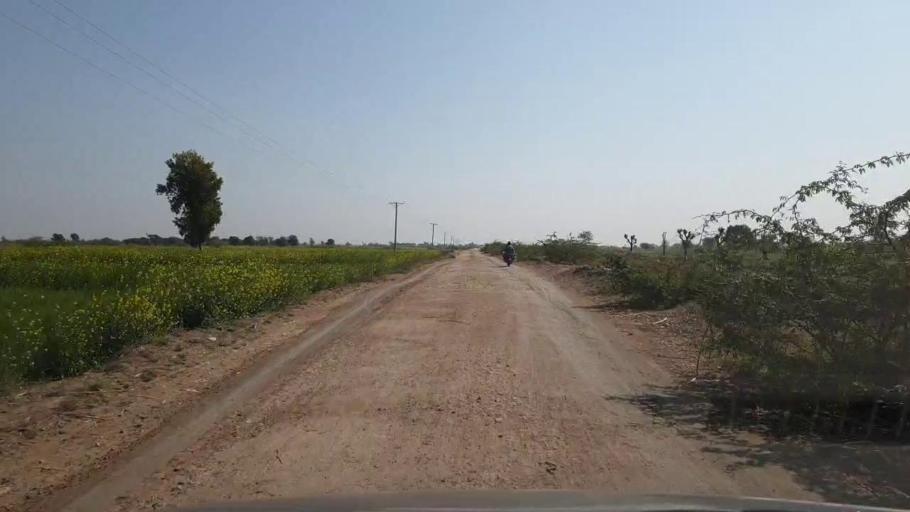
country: PK
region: Sindh
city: Samaro
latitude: 25.2538
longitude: 69.2689
